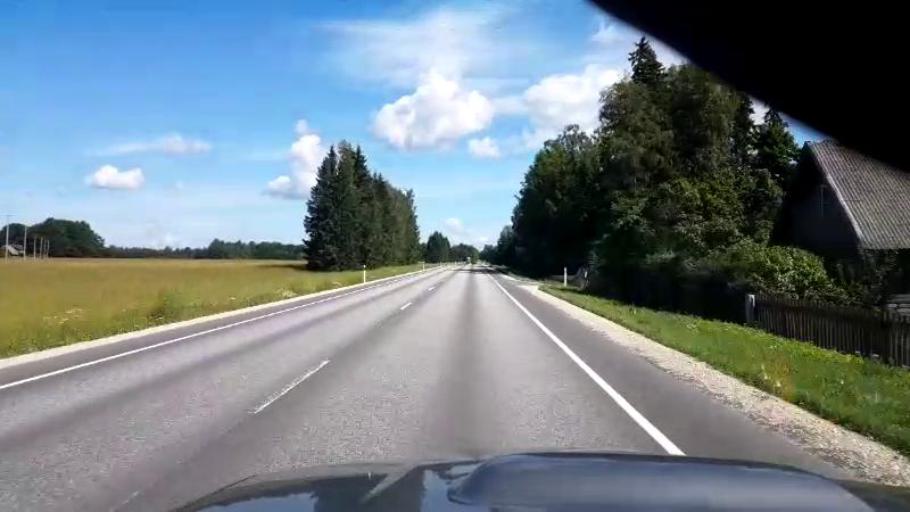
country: EE
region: Jaervamaa
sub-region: Paide linn
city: Paide
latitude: 58.9778
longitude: 25.6666
